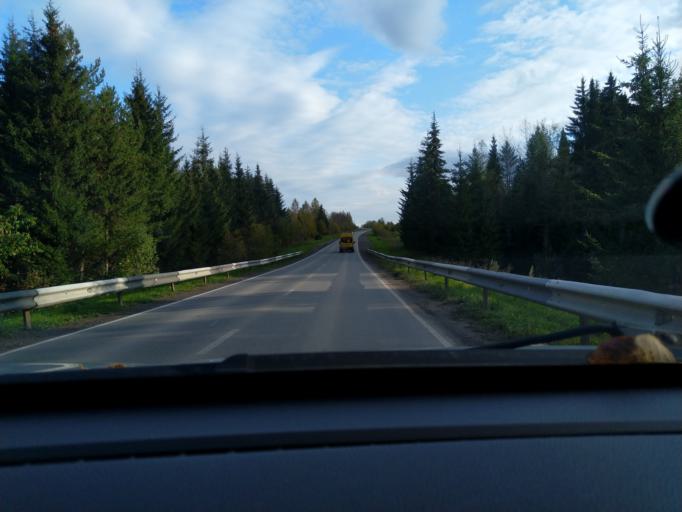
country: RU
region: Perm
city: Polazna
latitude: 58.2797
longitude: 56.4134
